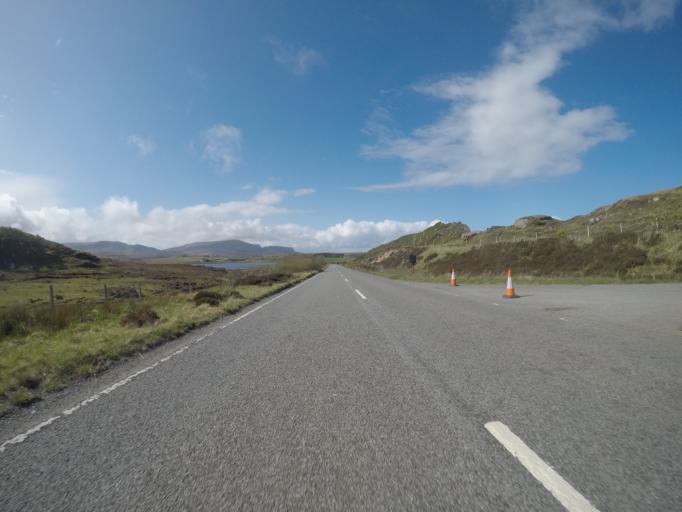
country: GB
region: Scotland
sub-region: Highland
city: Portree
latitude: 57.6026
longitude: -6.1676
